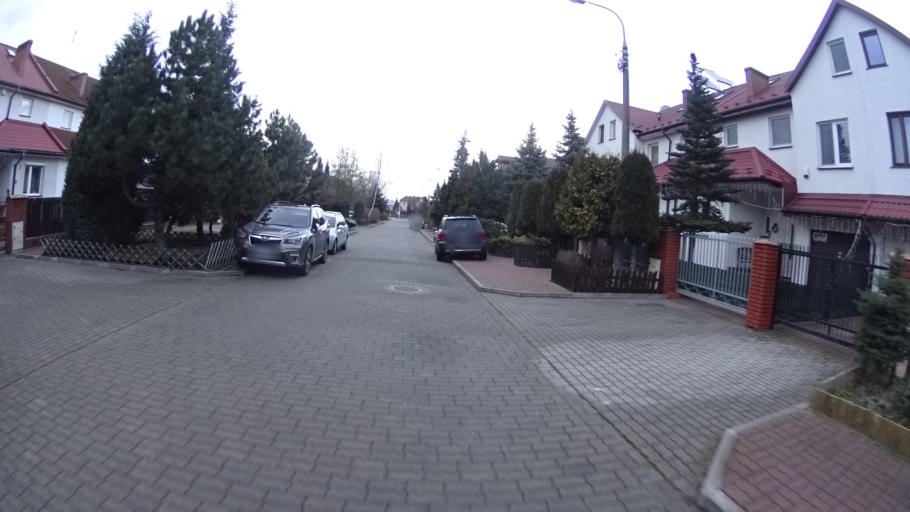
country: PL
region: Masovian Voivodeship
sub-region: Powiat pruszkowski
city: Nadarzyn
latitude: 52.1033
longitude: 20.7999
